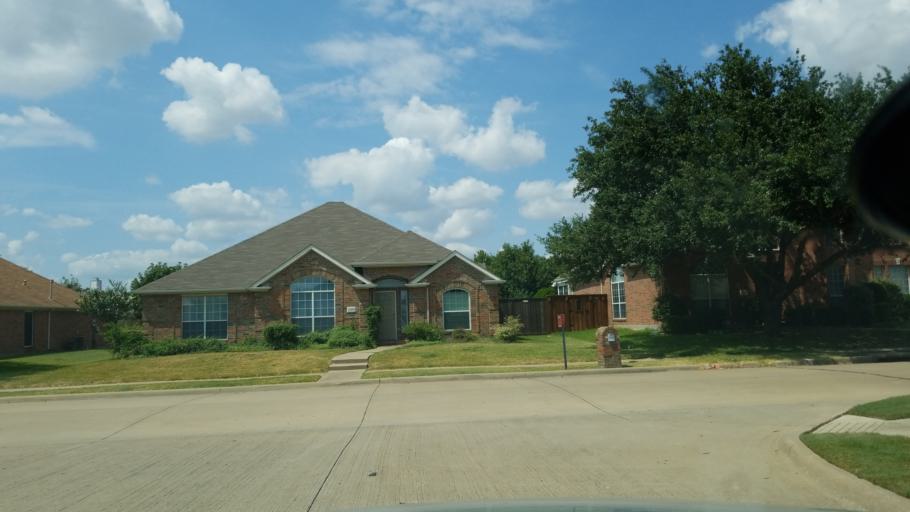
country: US
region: Texas
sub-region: Dallas County
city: Garland
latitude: 32.9256
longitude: -96.6617
